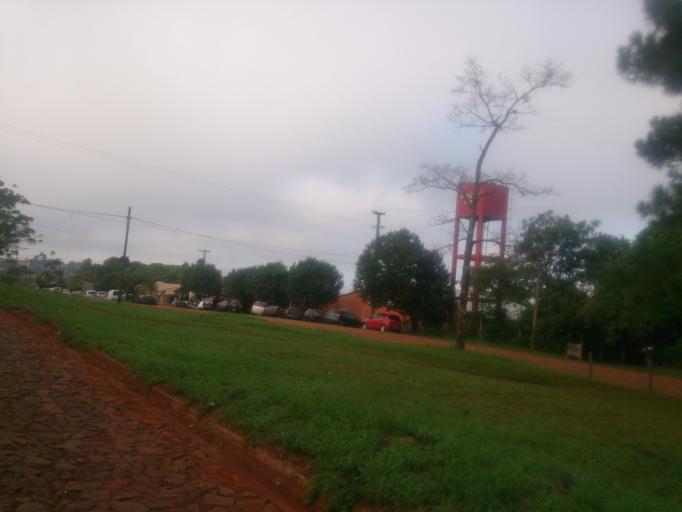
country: AR
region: Misiones
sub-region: Departamento de Obera
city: Obera
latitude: -27.4733
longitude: -55.1063
